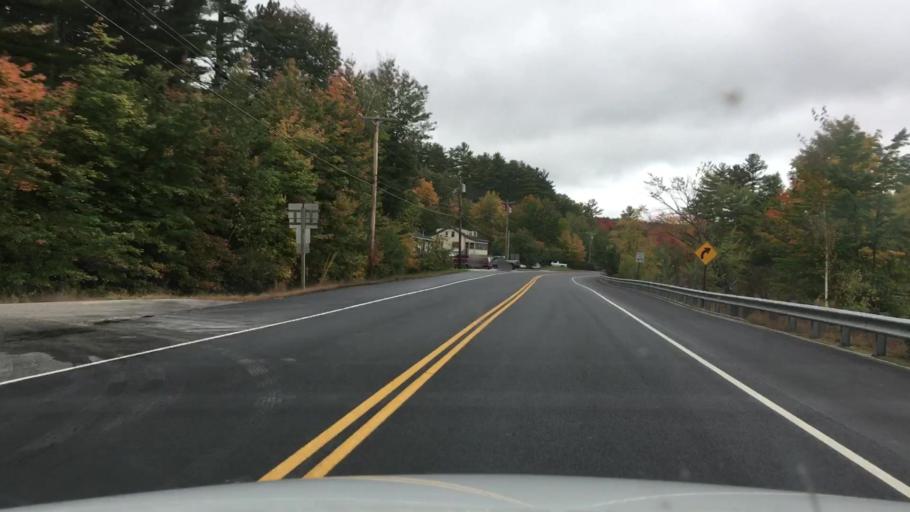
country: US
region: Maine
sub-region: Oxford County
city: Bethel
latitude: 44.4096
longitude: -70.8043
